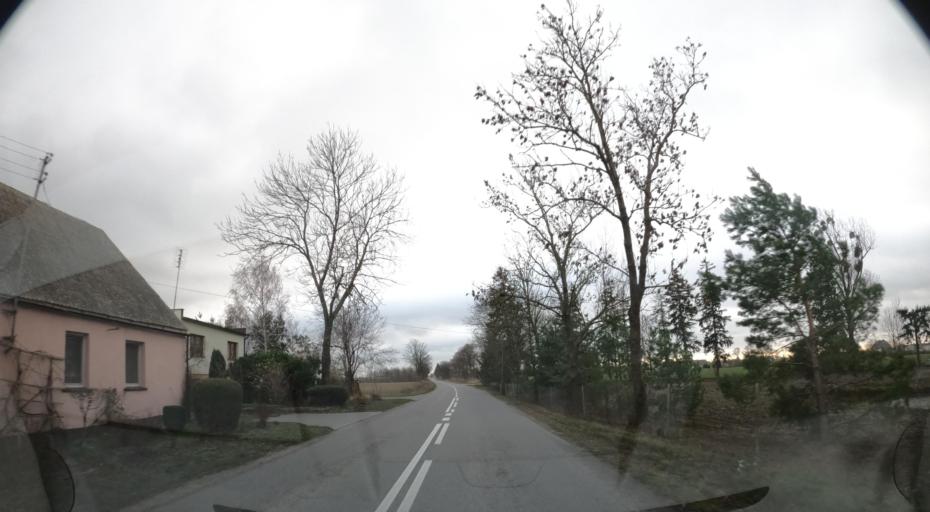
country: PL
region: Kujawsko-Pomorskie
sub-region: Powiat nakielski
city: Sadki
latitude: 53.1690
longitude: 17.4355
